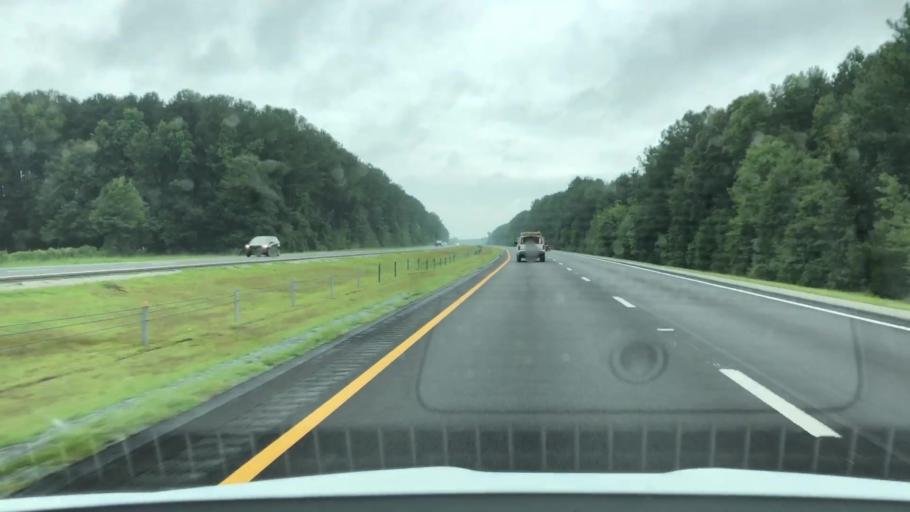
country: US
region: North Carolina
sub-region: Wayne County
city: Fremont
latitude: 35.4788
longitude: -77.9885
